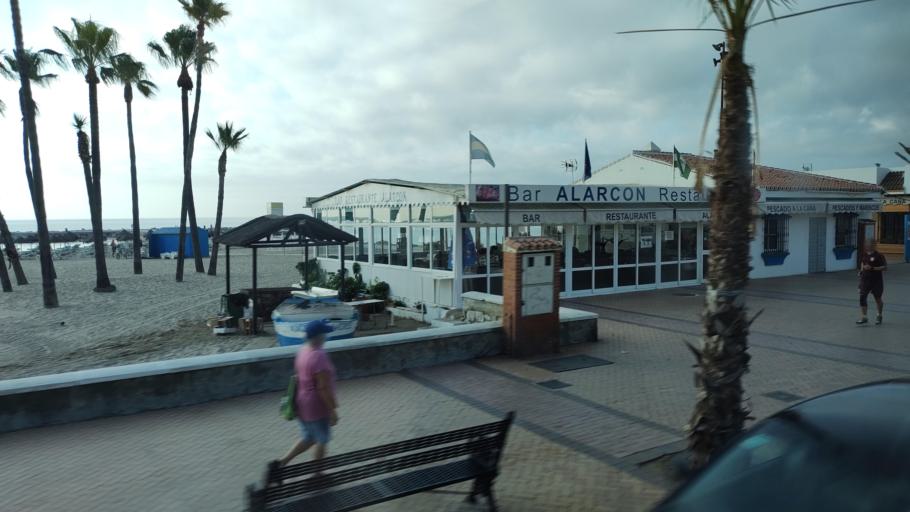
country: ES
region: Andalusia
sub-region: Provincia de Malaga
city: Fuengirola
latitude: 36.5467
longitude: -4.6166
